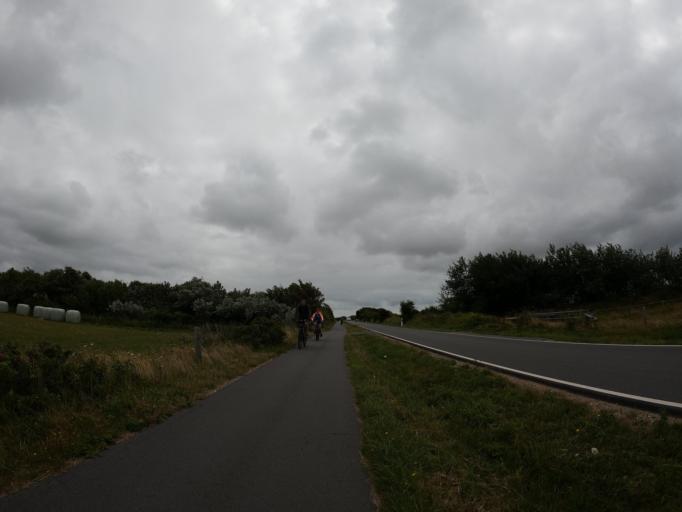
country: DE
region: Schleswig-Holstein
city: Tinnum
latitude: 54.9422
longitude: 8.3484
